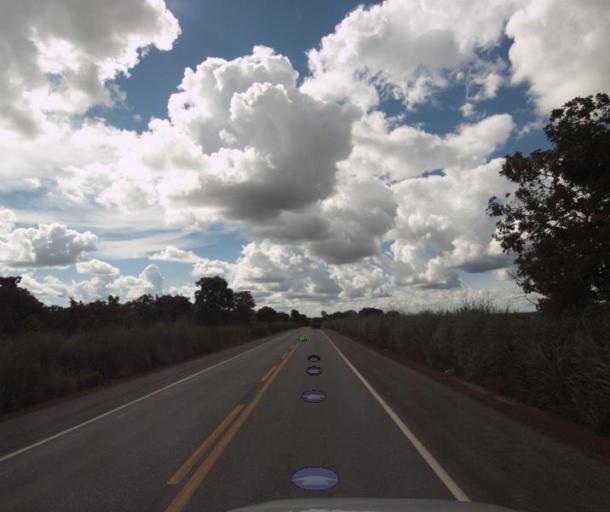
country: BR
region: Goias
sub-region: Porangatu
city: Porangatu
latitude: -13.3076
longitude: -49.1189
